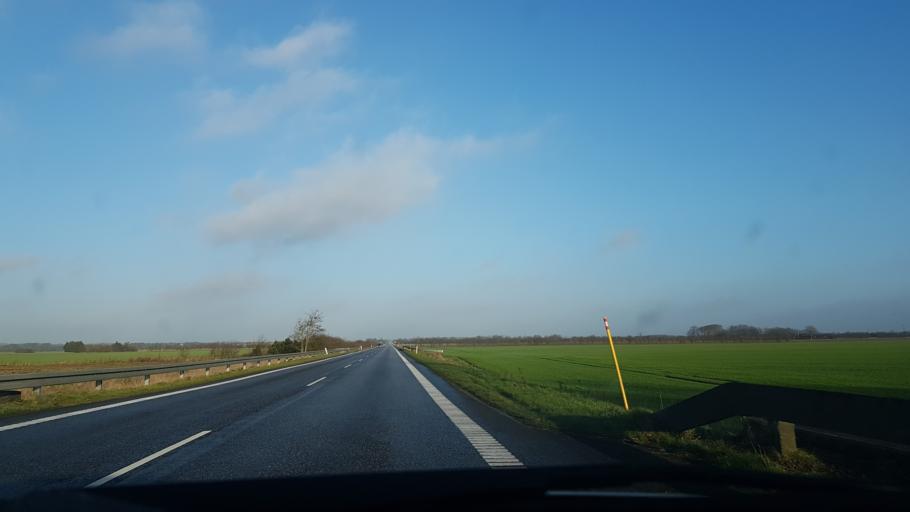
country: DK
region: South Denmark
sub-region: Tonder Kommune
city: Toftlund
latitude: 55.2173
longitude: 9.1036
